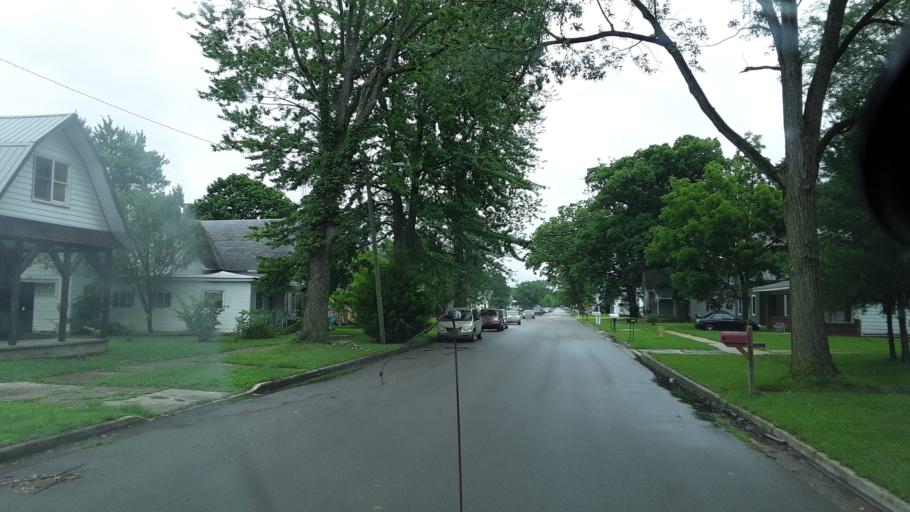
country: US
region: Indiana
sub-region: Jay County
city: Portland
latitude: 40.4362
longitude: -84.9857
